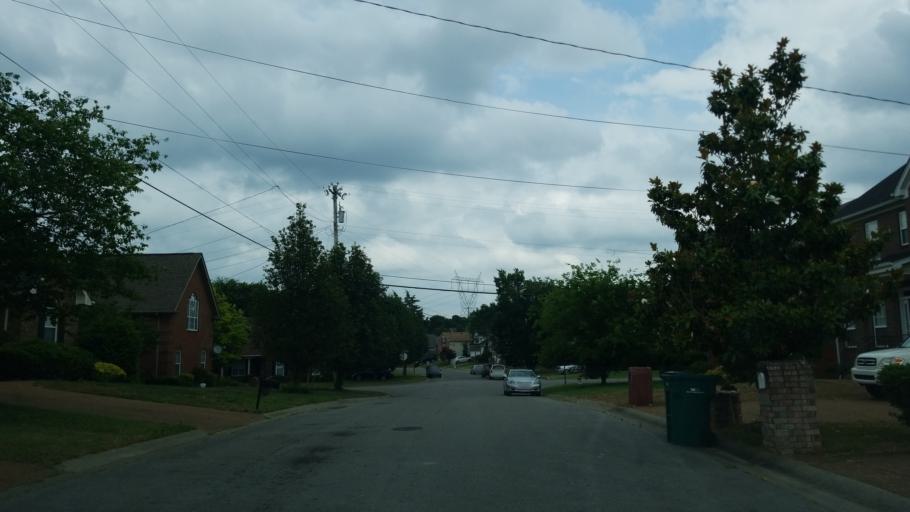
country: US
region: Tennessee
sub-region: Rutherford County
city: La Vergne
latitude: 36.0709
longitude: -86.5841
